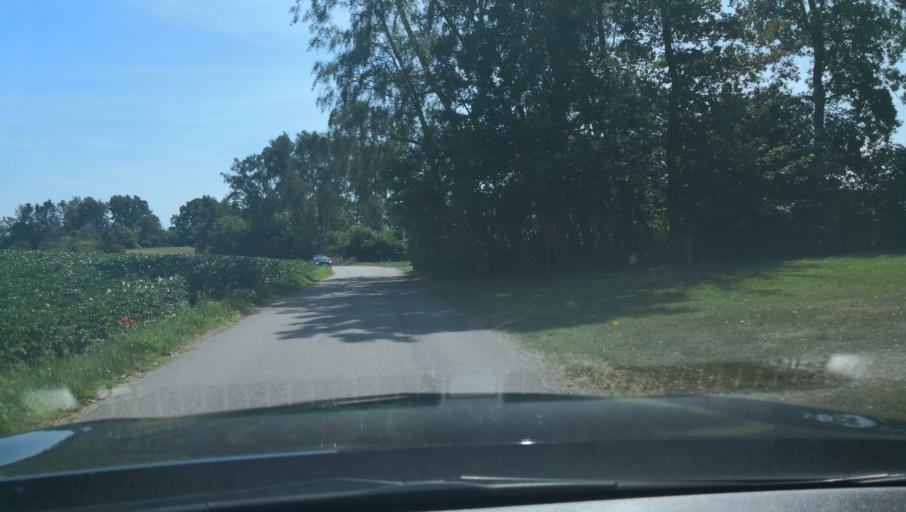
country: SE
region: Skane
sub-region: Ystads Kommun
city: Kopingebro
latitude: 55.3895
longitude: 14.1421
